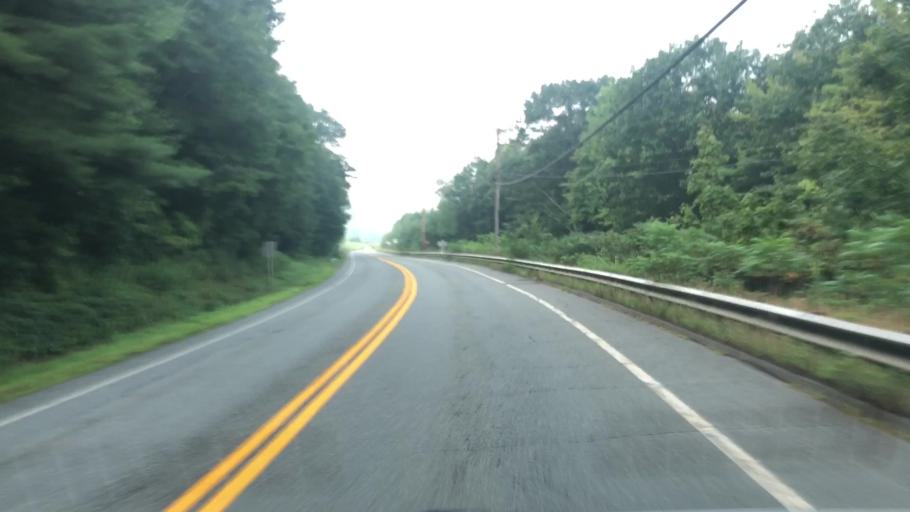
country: US
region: Massachusetts
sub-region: Franklin County
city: Buckland
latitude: 42.5800
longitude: -72.7997
